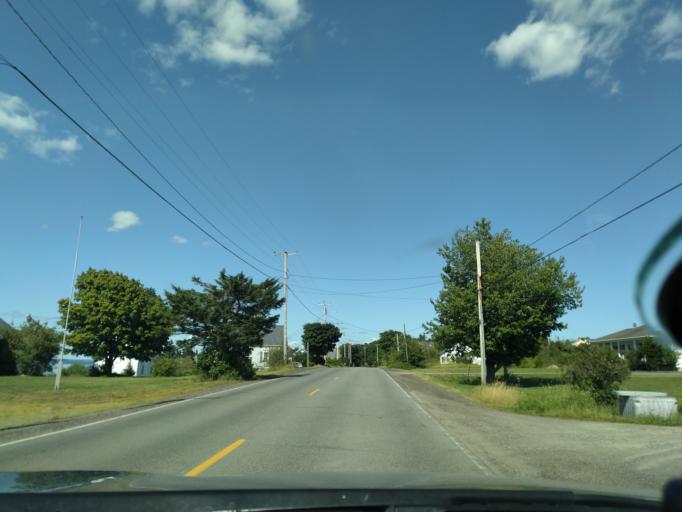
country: US
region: Maine
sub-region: Washington County
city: Eastport
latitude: 44.8511
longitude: -66.9975
